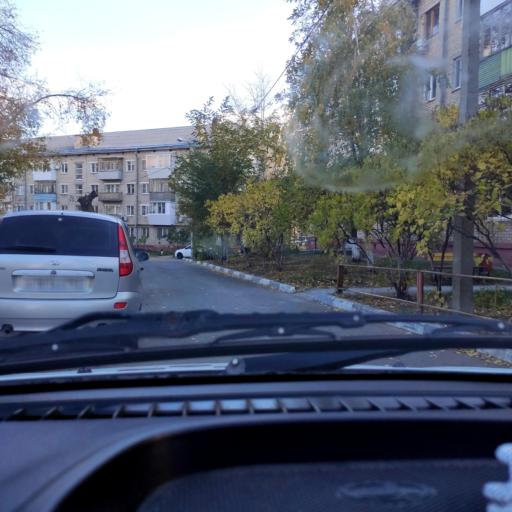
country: RU
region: Samara
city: Zhigulevsk
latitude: 53.4740
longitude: 49.4762
